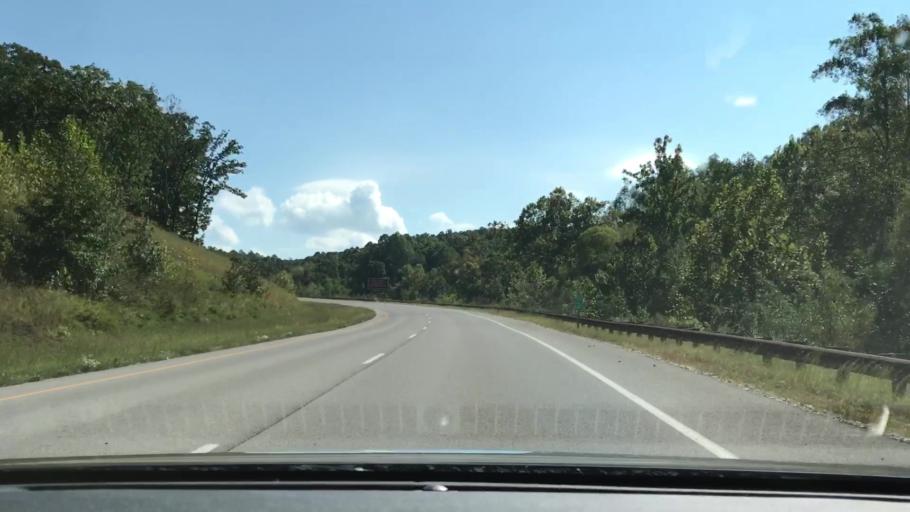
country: US
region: Kentucky
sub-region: Trigg County
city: Cadiz
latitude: 36.7779
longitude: -88.0881
